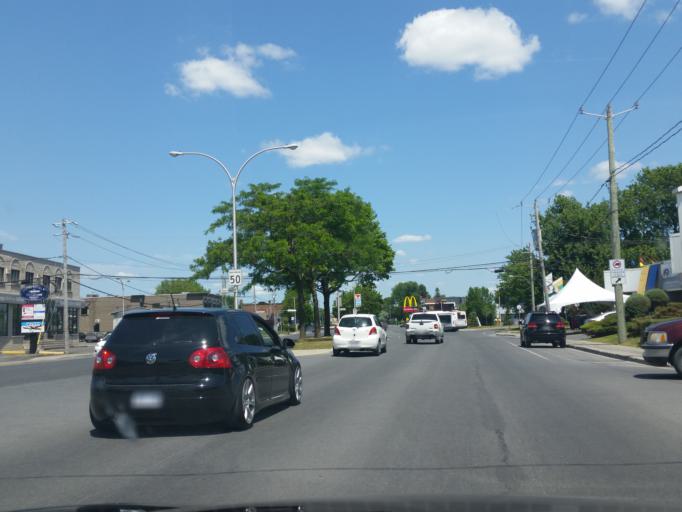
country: CA
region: Quebec
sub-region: Monteregie
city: Saint-Jean-sur-Richelieu
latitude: 45.3175
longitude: -73.2641
